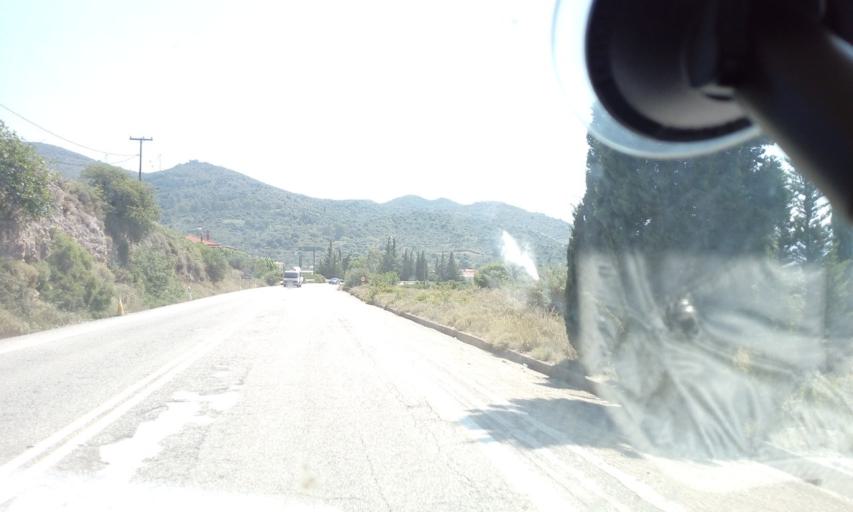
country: GR
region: West Greece
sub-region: Nomos Aitolias kai Akarnanias
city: Antirrio
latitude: 38.3556
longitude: 21.7007
